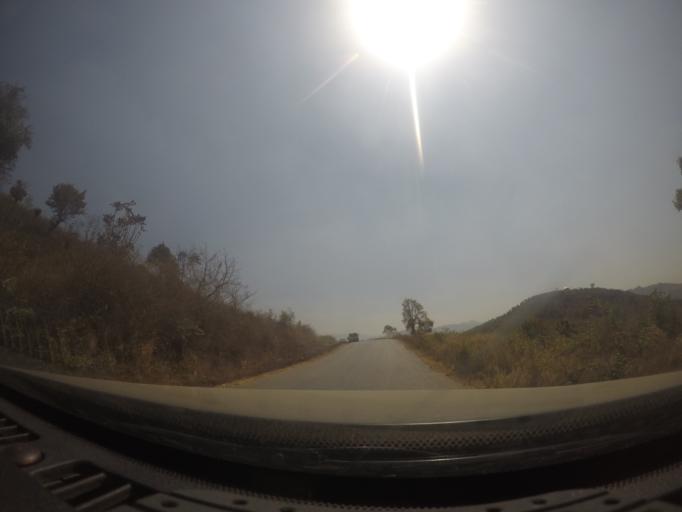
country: MM
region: Shan
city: Taunggyi
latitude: 20.8045
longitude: 97.2564
